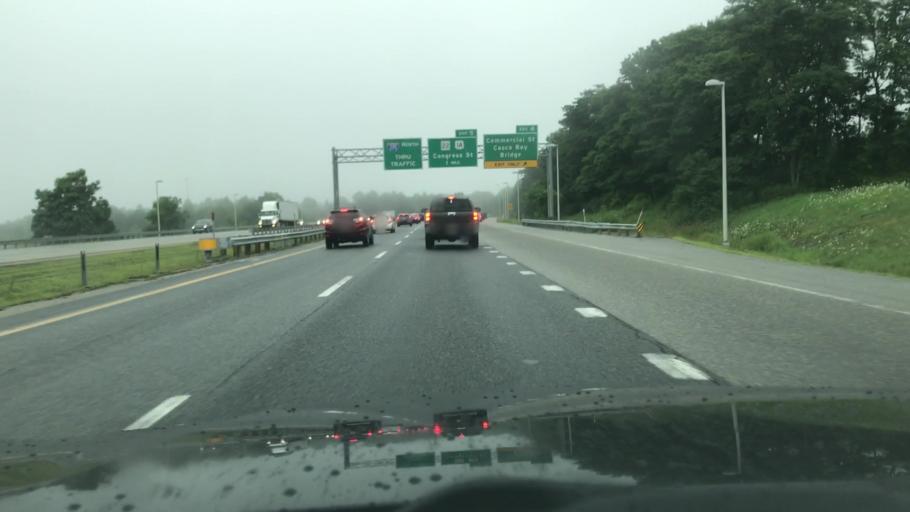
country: US
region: Maine
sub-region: Cumberland County
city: South Portland Gardens
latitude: 43.6355
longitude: -70.3005
